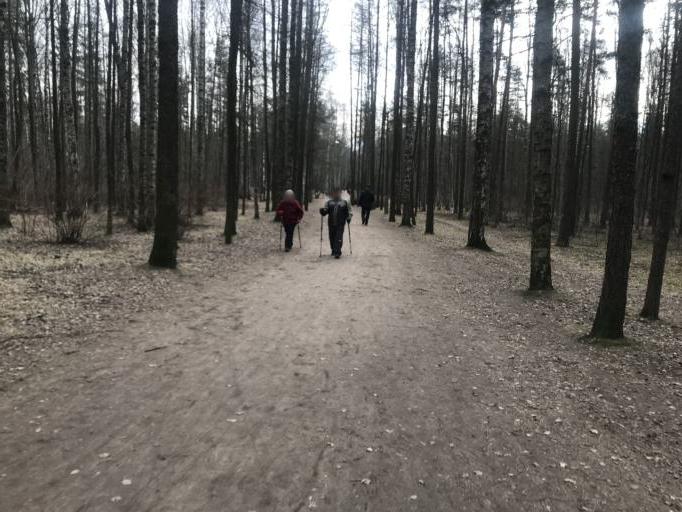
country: RU
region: St.-Petersburg
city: Sosnovka
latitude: 60.0182
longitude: 30.3458
